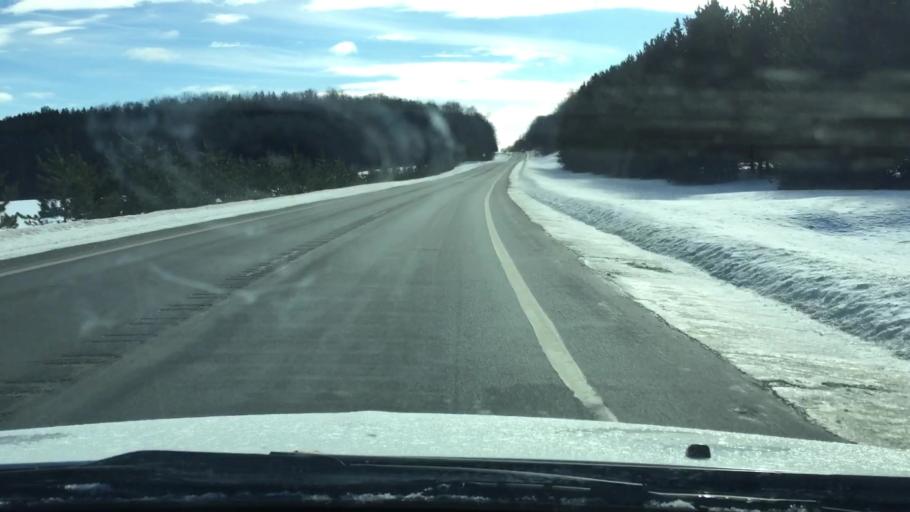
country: US
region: Michigan
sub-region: Antrim County
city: Mancelona
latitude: 44.9803
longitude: -85.0537
